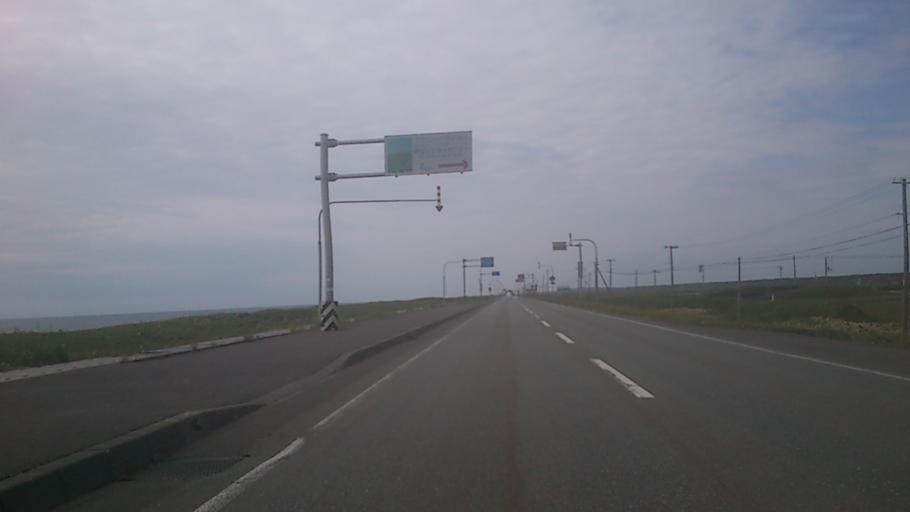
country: JP
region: Hokkaido
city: Makubetsu
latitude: 44.9921
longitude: 141.6870
